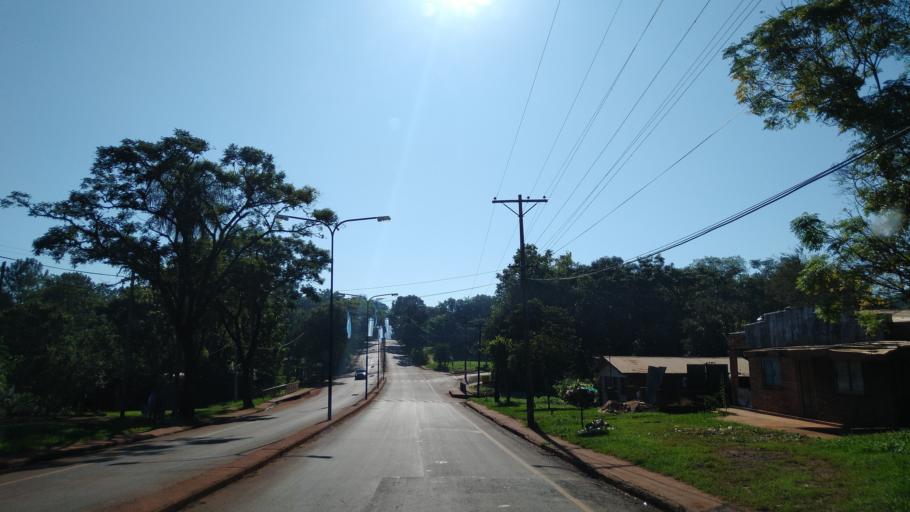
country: AR
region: Misiones
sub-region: Departamento de Montecarlo
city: Montecarlo
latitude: -26.5713
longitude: -54.7298
